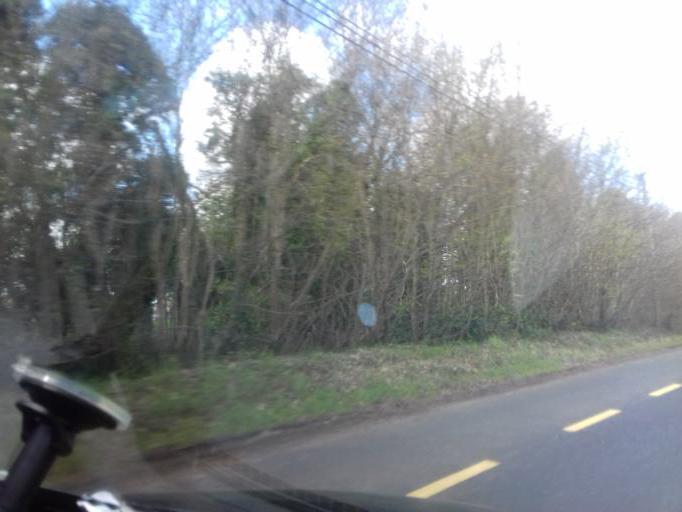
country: IE
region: Ulster
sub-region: An Cabhan
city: Ballyjamesduff
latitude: 53.9711
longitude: -7.2418
